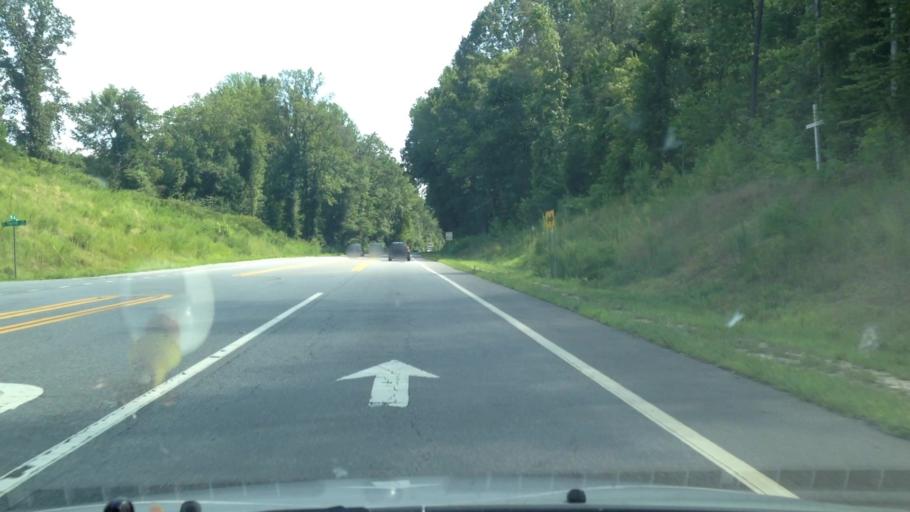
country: US
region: North Carolina
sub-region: Guilford County
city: Oak Ridge
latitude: 36.1965
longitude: -79.9852
